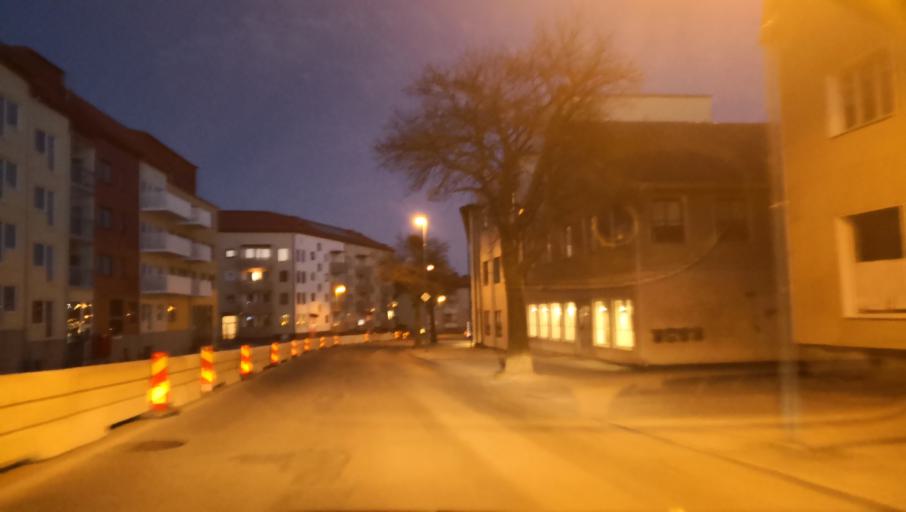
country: SE
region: Stockholm
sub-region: Nynashamns Kommun
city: Nynashamn
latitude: 58.9114
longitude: 17.9513
